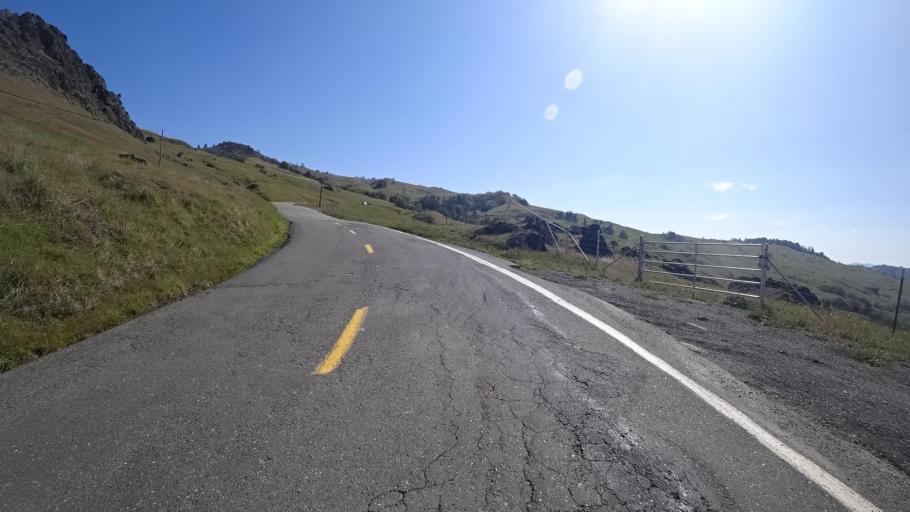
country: US
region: California
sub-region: Humboldt County
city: Redway
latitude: 40.1045
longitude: -123.7051
